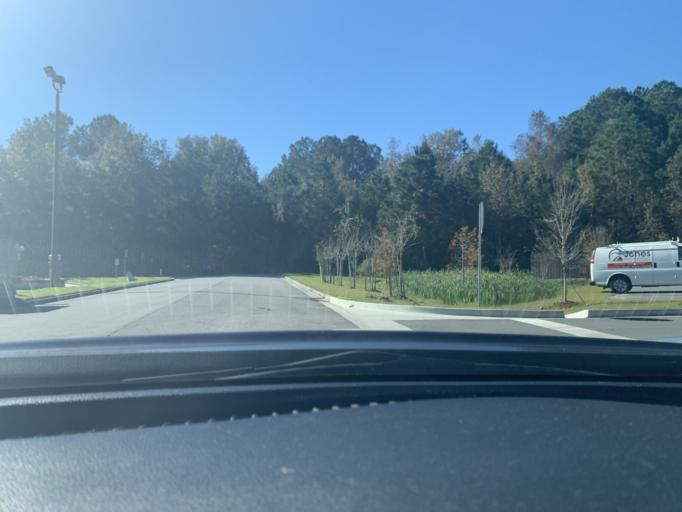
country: US
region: Georgia
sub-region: Chatham County
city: Pooler
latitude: 32.1308
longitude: -81.2585
